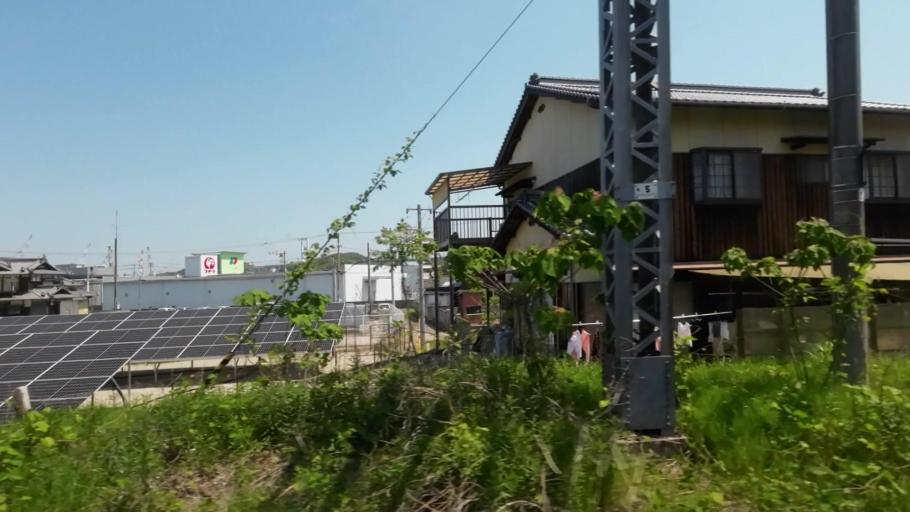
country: JP
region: Ehime
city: Hojo
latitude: 34.0971
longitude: 132.9707
